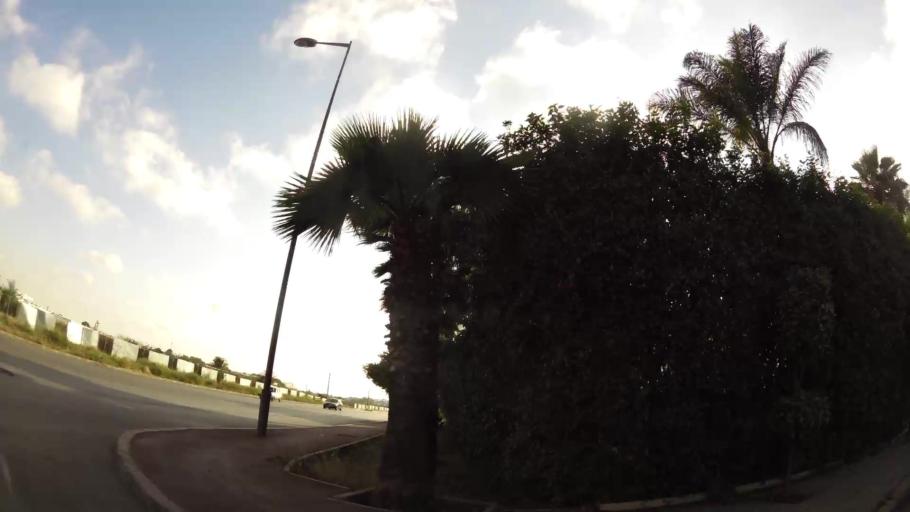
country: MA
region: Rabat-Sale-Zemmour-Zaer
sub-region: Rabat
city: Rabat
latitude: 33.9575
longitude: -6.8516
